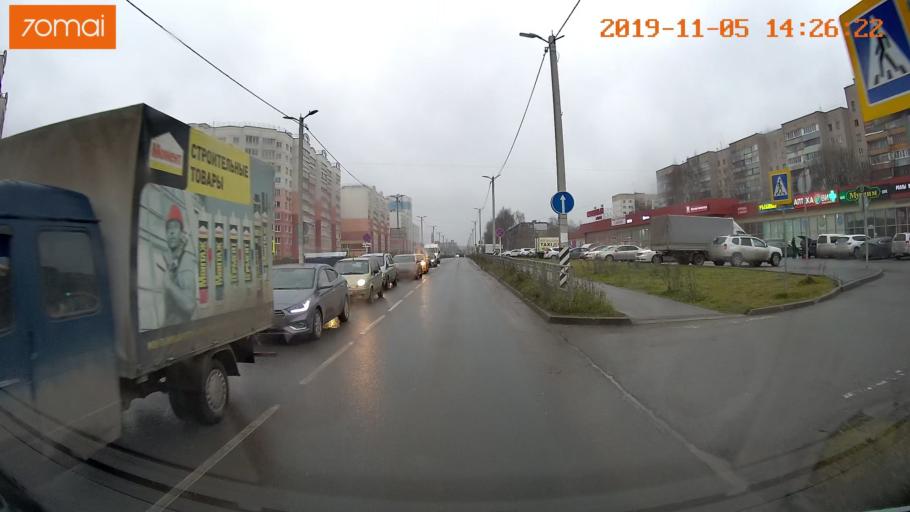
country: RU
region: Ivanovo
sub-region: Gorod Ivanovo
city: Ivanovo
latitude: 56.9709
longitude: 40.9853
